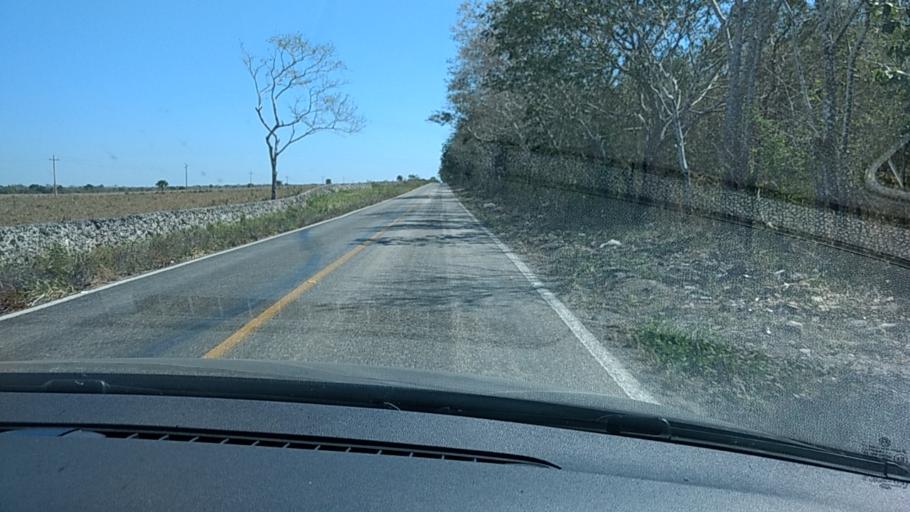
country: MX
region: Yucatan
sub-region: Tizimin
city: Tizimin
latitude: 21.2026
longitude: -88.1933
